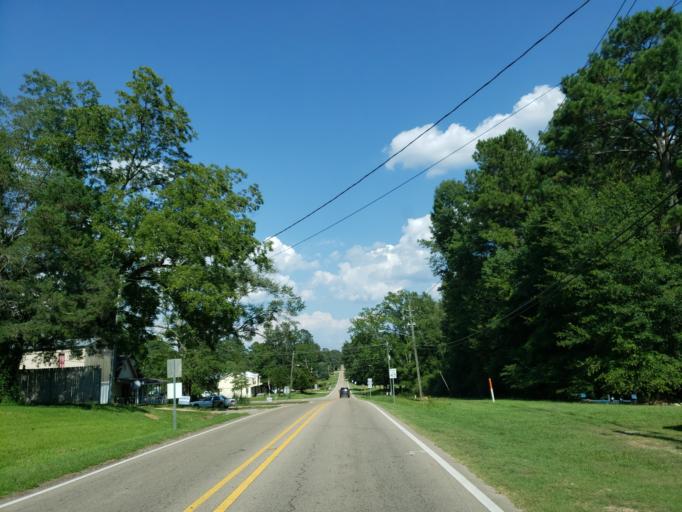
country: US
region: Mississippi
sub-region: Covington County
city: Collins
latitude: 31.5618
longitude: -89.4937
